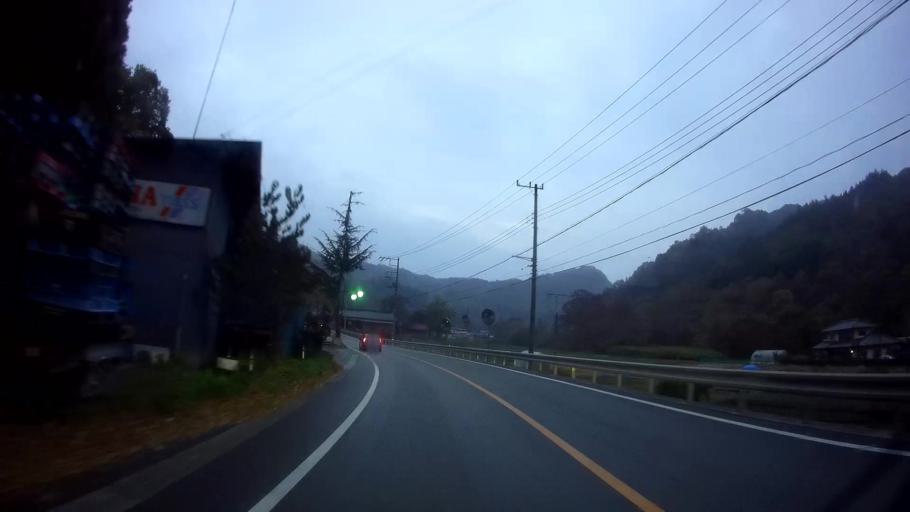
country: JP
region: Gunma
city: Nakanojomachi
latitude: 36.5263
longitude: 138.7815
